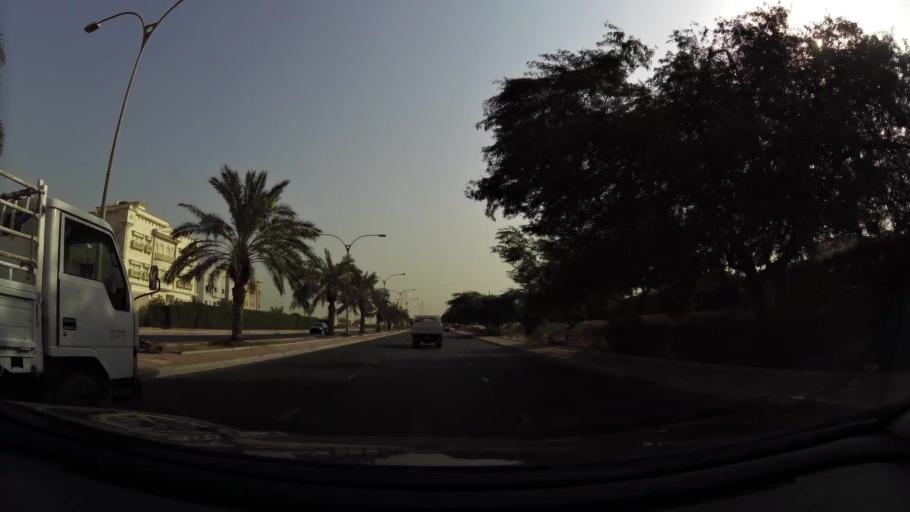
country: KW
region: Al Ahmadi
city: Ar Riqqah
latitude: 29.1236
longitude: 48.1046
